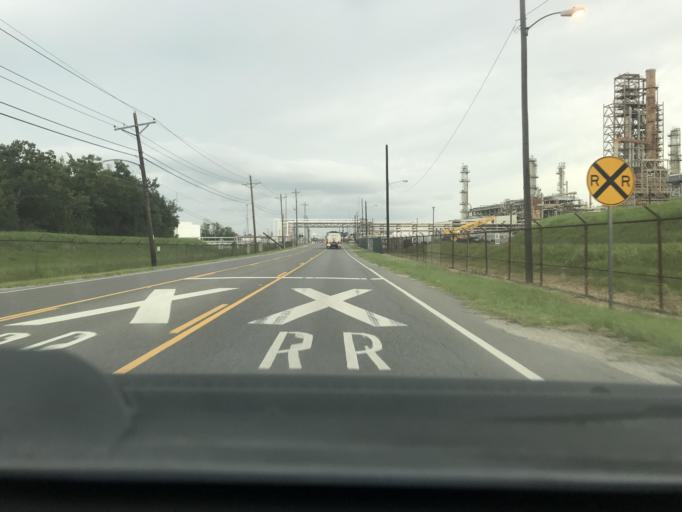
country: US
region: Louisiana
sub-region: Calcasieu Parish
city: Westlake
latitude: 30.2453
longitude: -93.2780
